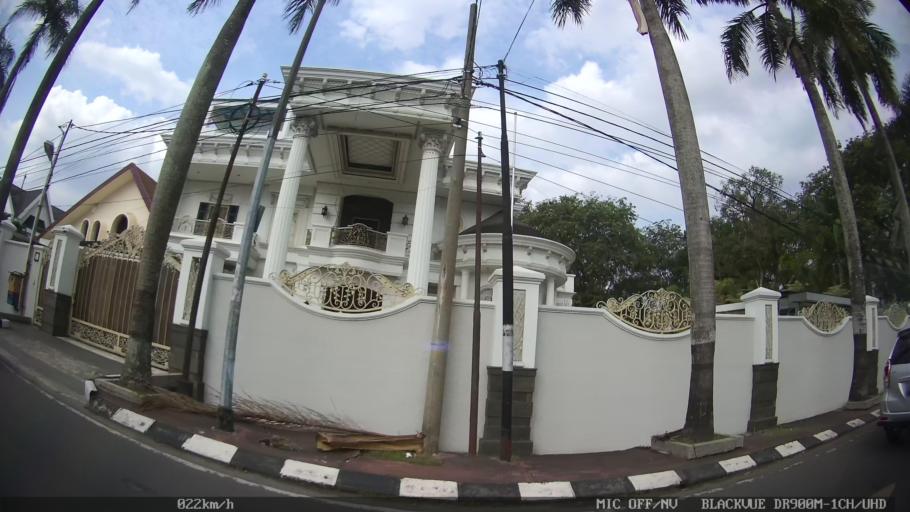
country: ID
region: North Sumatra
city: Medan
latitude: 3.5739
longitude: 98.6708
